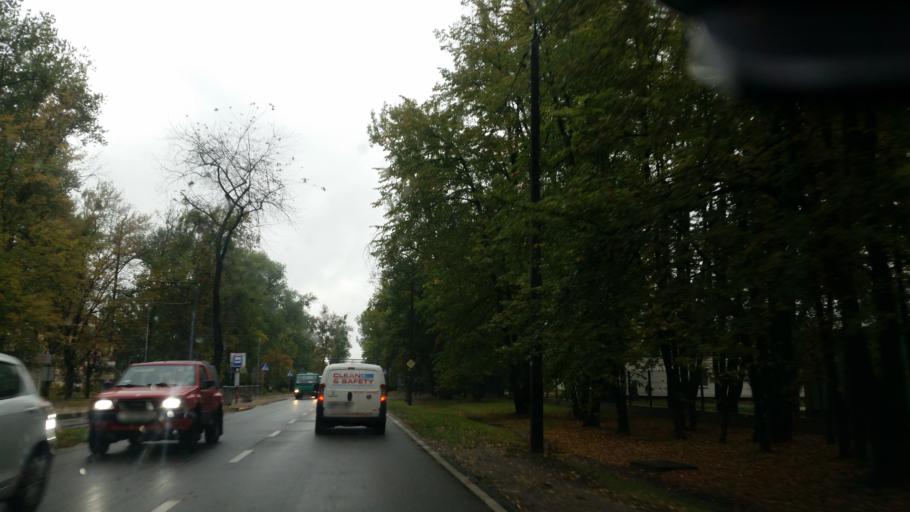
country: PL
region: Masovian Voivodeship
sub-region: Warszawa
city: Bemowo
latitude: 52.2553
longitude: 20.8981
